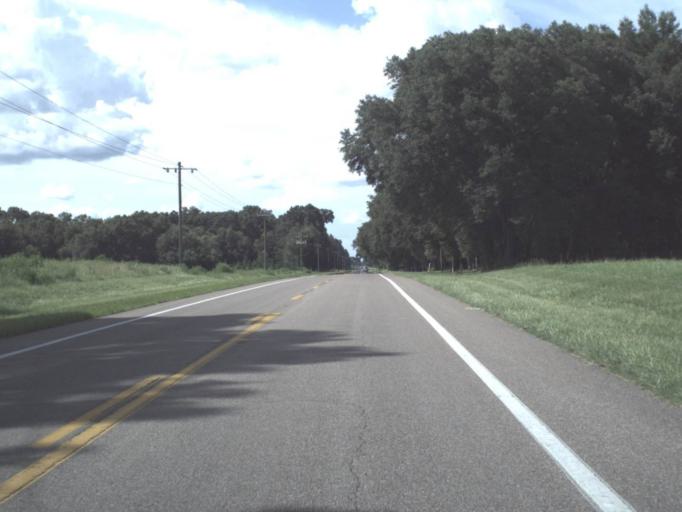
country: US
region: Florida
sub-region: Gilchrist County
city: Trenton
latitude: 29.6829
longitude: -82.8573
